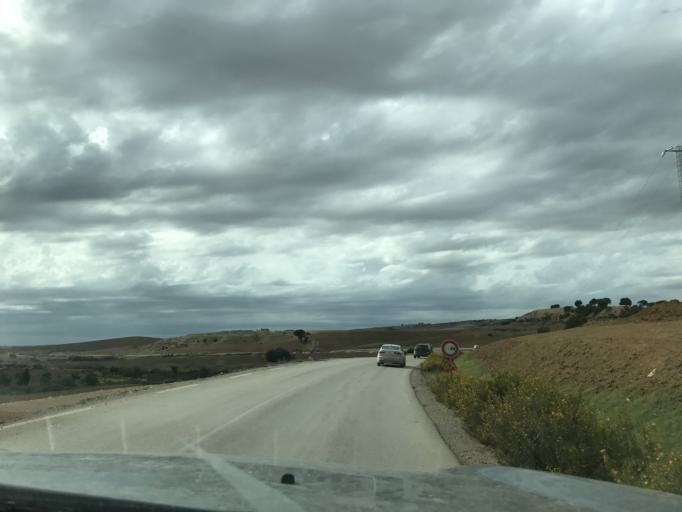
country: TN
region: Silyanah
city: Bu `Aradah
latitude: 36.1809
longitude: 9.6723
